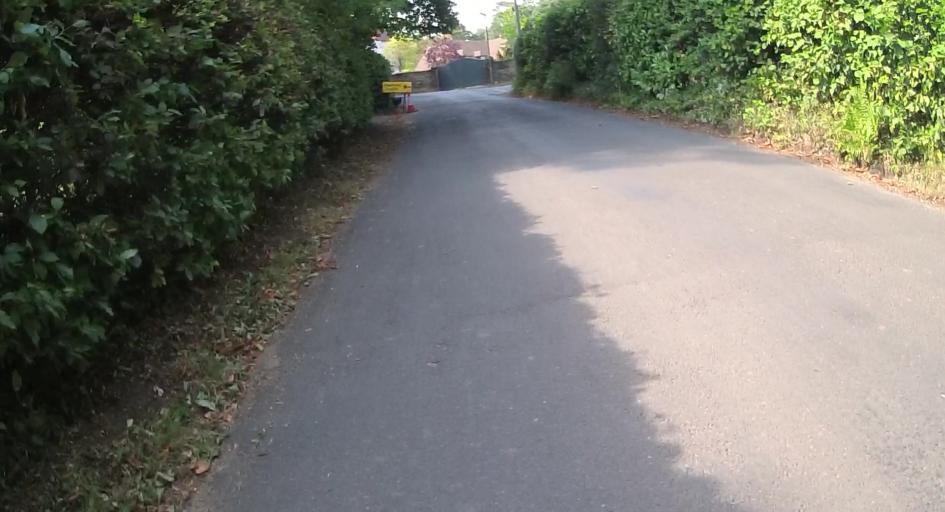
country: GB
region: England
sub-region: Surrey
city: Farnham
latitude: 51.1965
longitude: -0.8011
